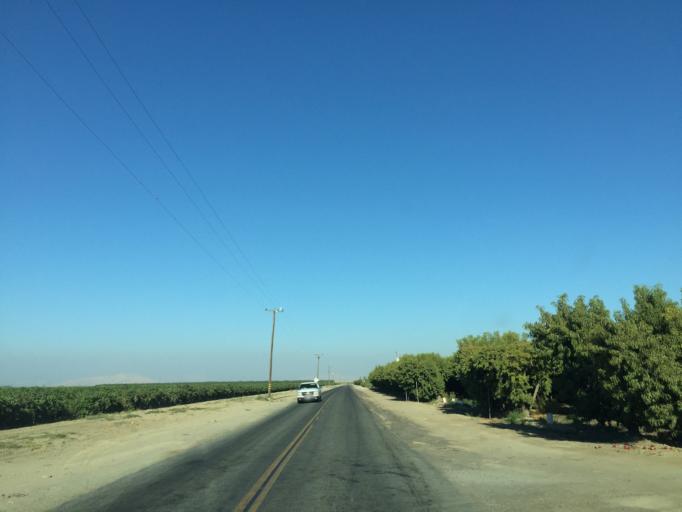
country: US
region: California
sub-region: Tulare County
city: London
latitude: 36.4589
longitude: -119.4388
